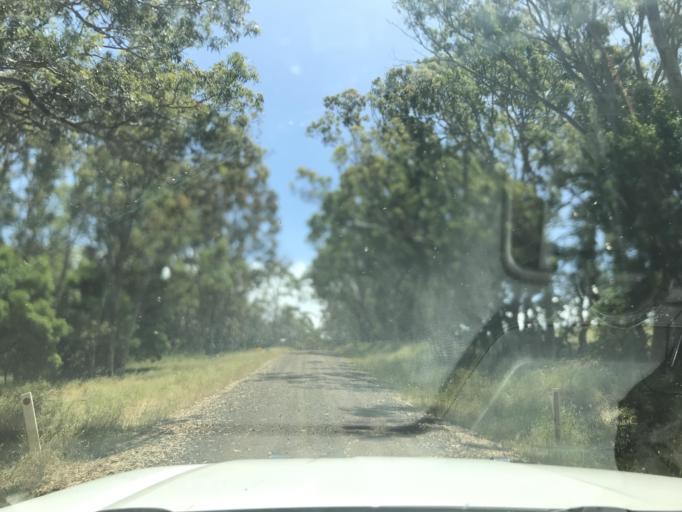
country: AU
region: South Australia
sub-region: Wattle Range
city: Penola
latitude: -37.2882
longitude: 141.4815
